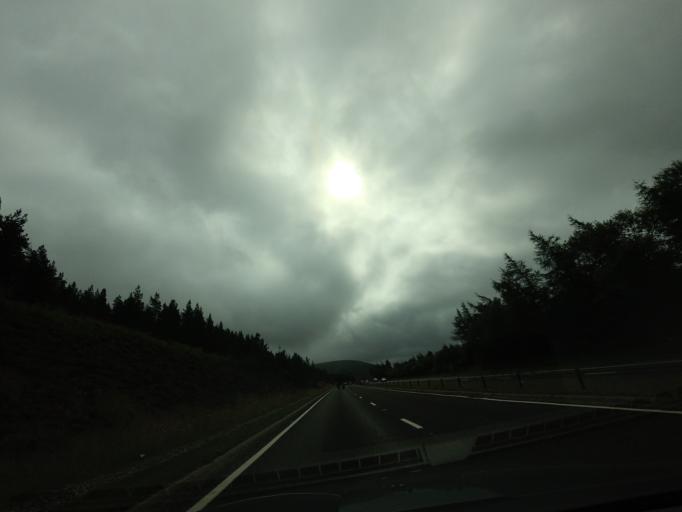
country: GB
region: Scotland
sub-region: Highland
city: Aviemore
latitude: 57.3129
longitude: -3.9524
